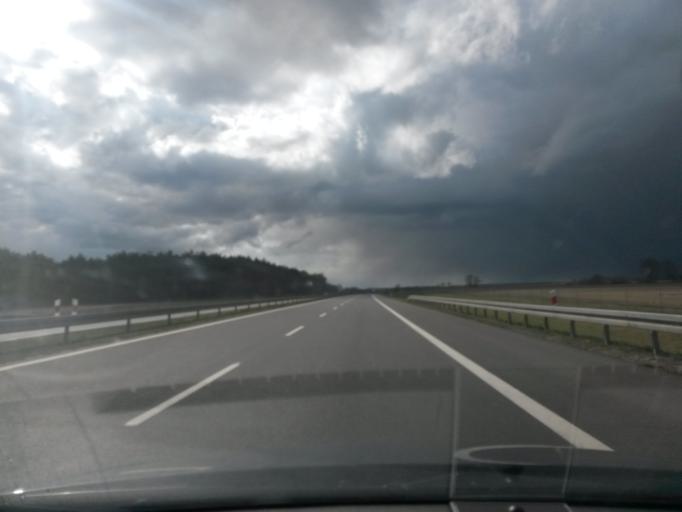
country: PL
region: Greater Poland Voivodeship
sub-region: Powiat sredzki
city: Dominowo
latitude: 52.3109
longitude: 17.3723
